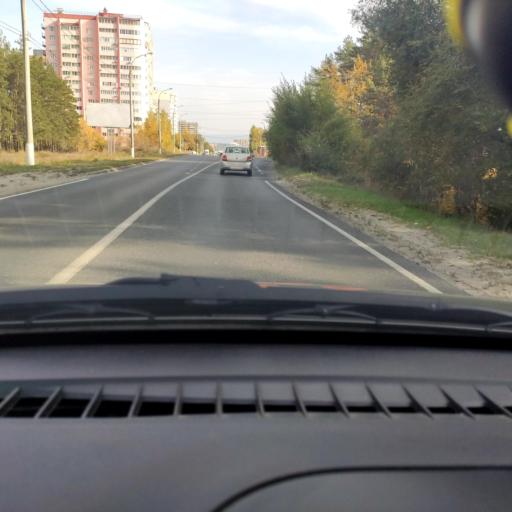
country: RU
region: Samara
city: Zhigulevsk
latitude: 53.4771
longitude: 49.4505
